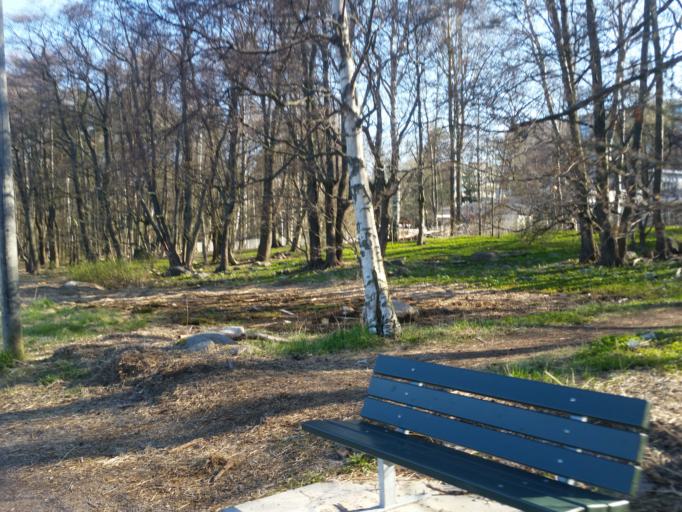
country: FI
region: Uusimaa
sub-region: Helsinki
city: Teekkarikylae
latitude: 60.1523
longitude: 24.8750
